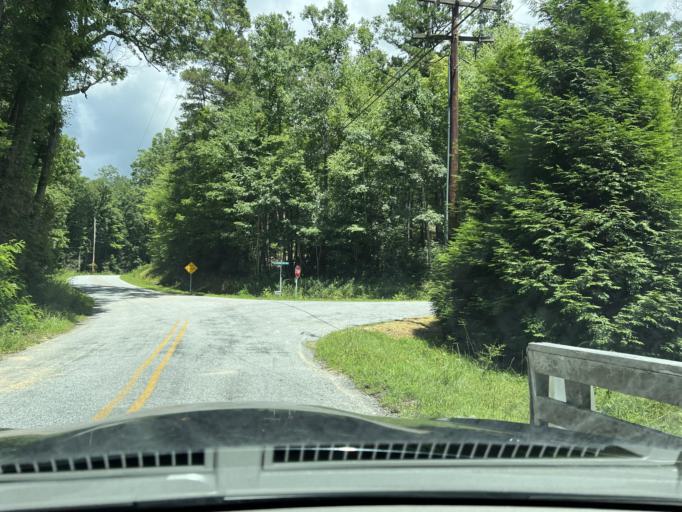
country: US
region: North Carolina
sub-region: Henderson County
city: Fruitland
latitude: 35.4183
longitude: -82.4054
